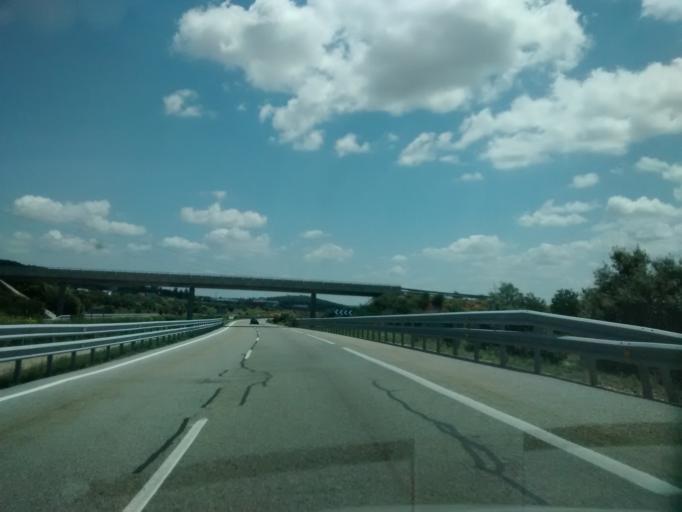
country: ES
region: Castille and Leon
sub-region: Provincia de Leon
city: Brazuelo
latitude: 42.4848
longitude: -6.1188
